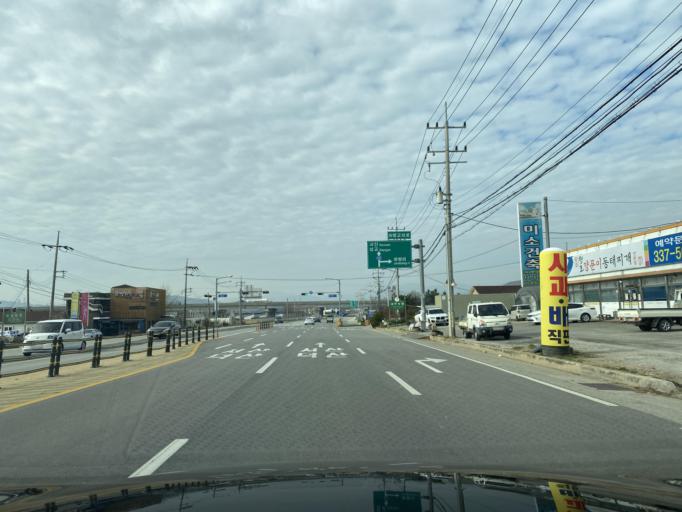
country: KR
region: Chungcheongnam-do
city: Yesan
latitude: 36.6861
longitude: 126.7751
